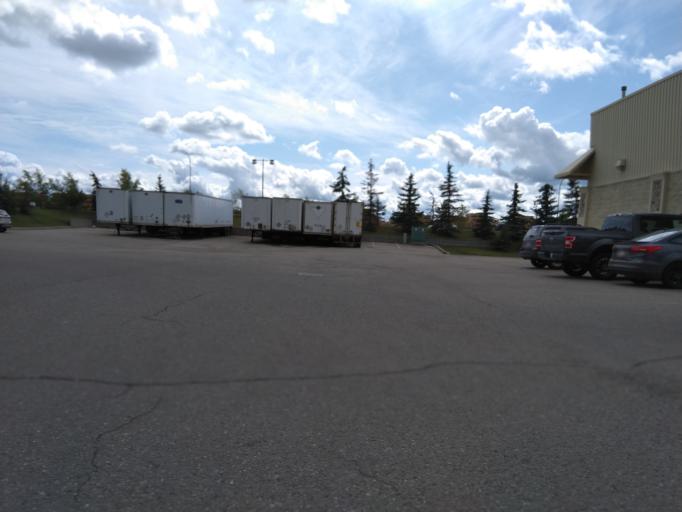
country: CA
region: Alberta
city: Cochrane
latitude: 51.1840
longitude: -114.4753
